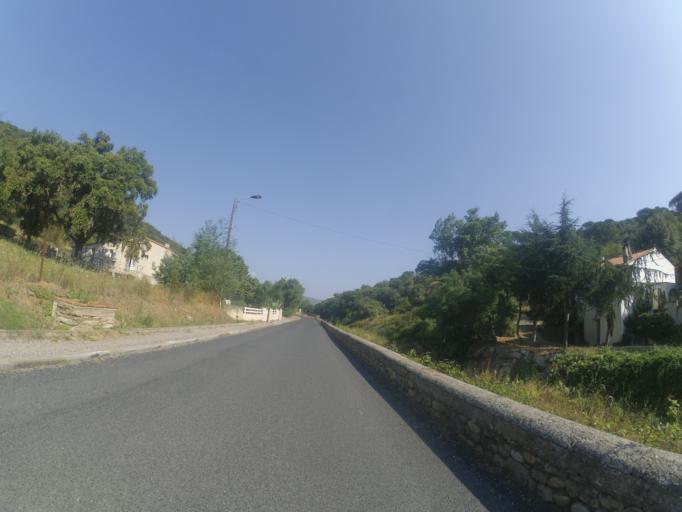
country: FR
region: Languedoc-Roussillon
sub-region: Departement des Pyrenees-Orientales
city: Ille-sur-Tet
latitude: 42.6487
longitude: 2.6247
